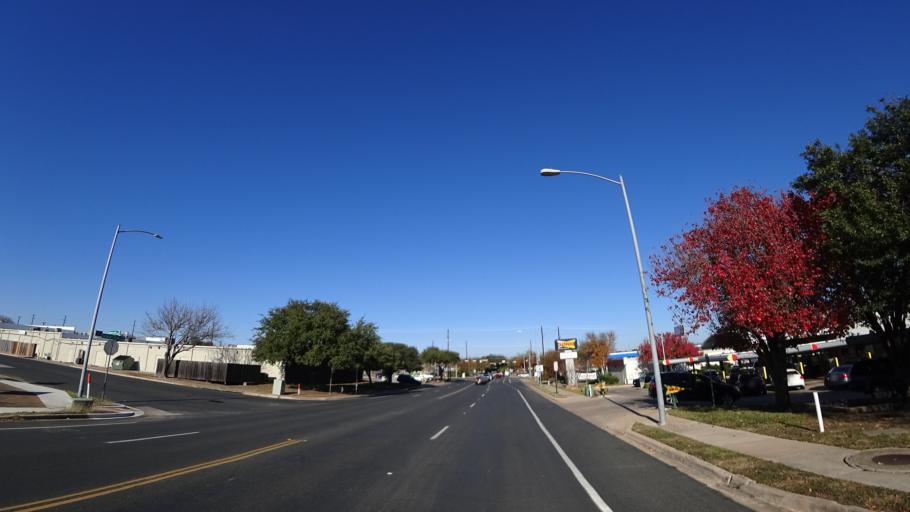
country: US
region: Texas
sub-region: Travis County
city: Wells Branch
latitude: 30.4147
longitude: -97.6966
